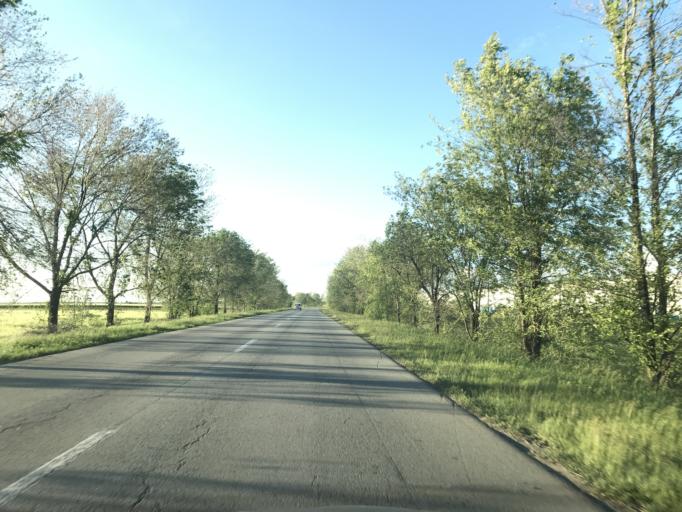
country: RS
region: Autonomna Pokrajina Vojvodina
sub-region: Srednjebanatski Okrug
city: Zrenjanin
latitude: 45.3862
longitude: 20.3521
